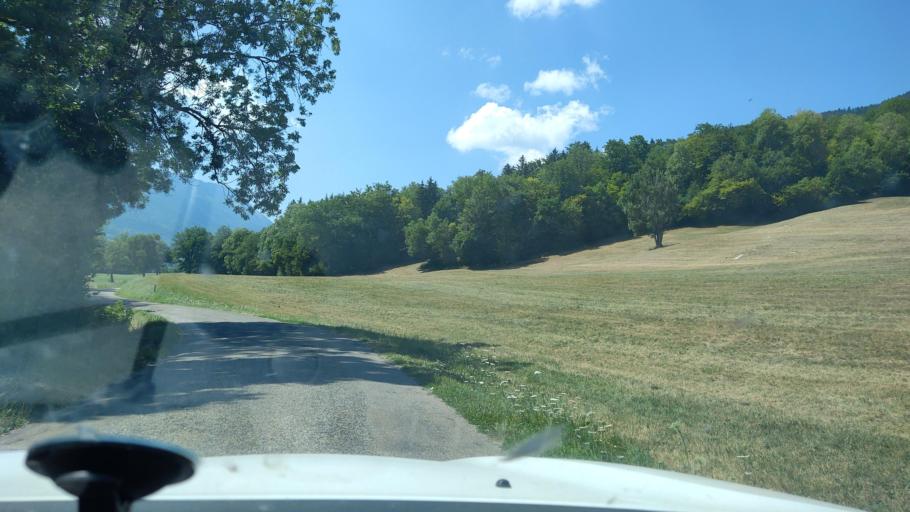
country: FR
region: Rhone-Alpes
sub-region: Departement de la Haute-Savoie
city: Cusy
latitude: 45.7060
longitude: 6.0801
